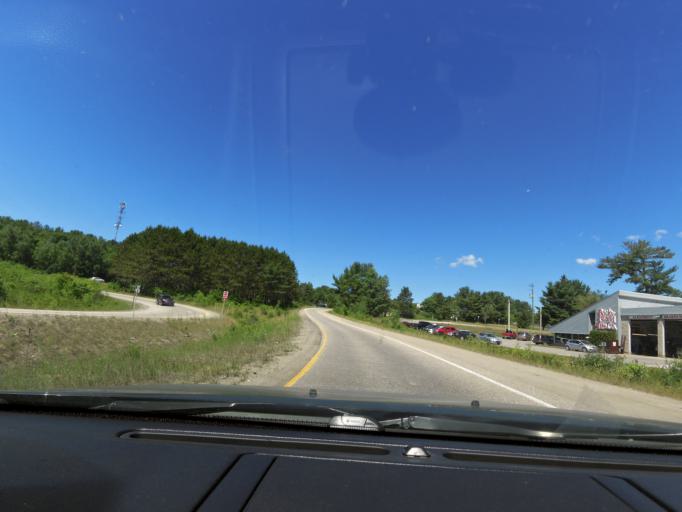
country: CA
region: Ontario
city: Bracebridge
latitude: 45.0546
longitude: -79.2886
